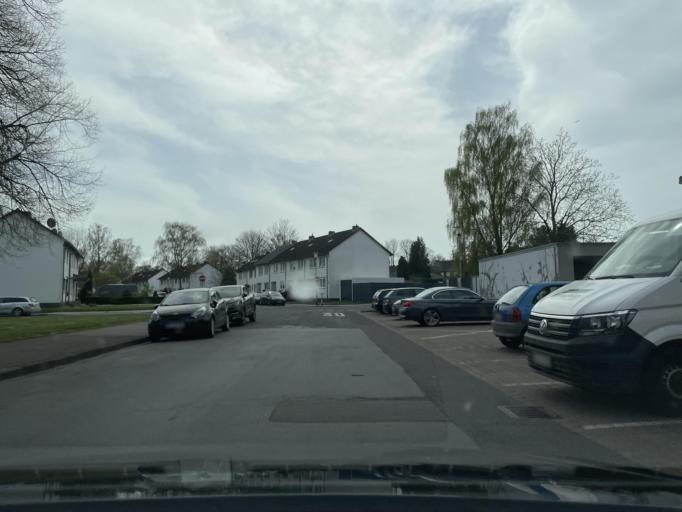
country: DE
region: North Rhine-Westphalia
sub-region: Regierungsbezirk Dusseldorf
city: Monchengladbach
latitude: 51.2048
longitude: 6.4141
